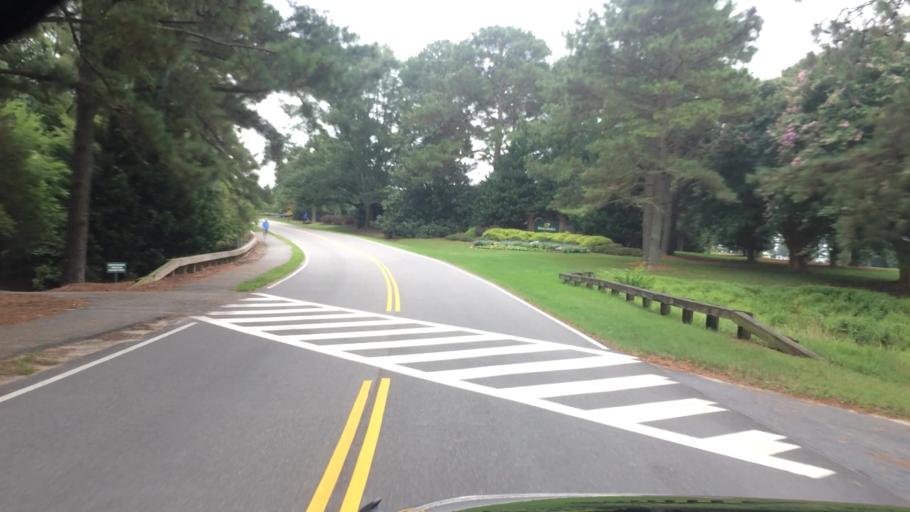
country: US
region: Virginia
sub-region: City of Williamsburg
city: Williamsburg
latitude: 37.2293
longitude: -76.6656
